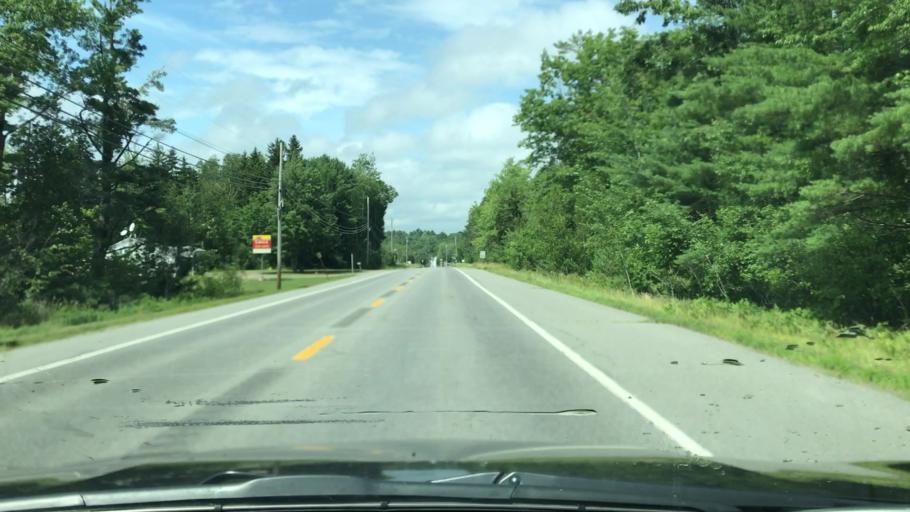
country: US
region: Maine
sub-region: Waldo County
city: Northport
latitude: 44.3771
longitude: -68.9848
